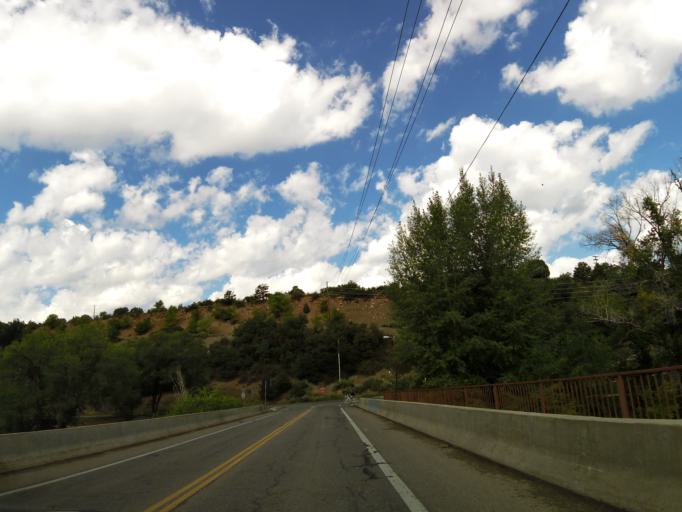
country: US
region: Colorado
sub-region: La Plata County
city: Durango
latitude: 37.2742
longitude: -107.8843
